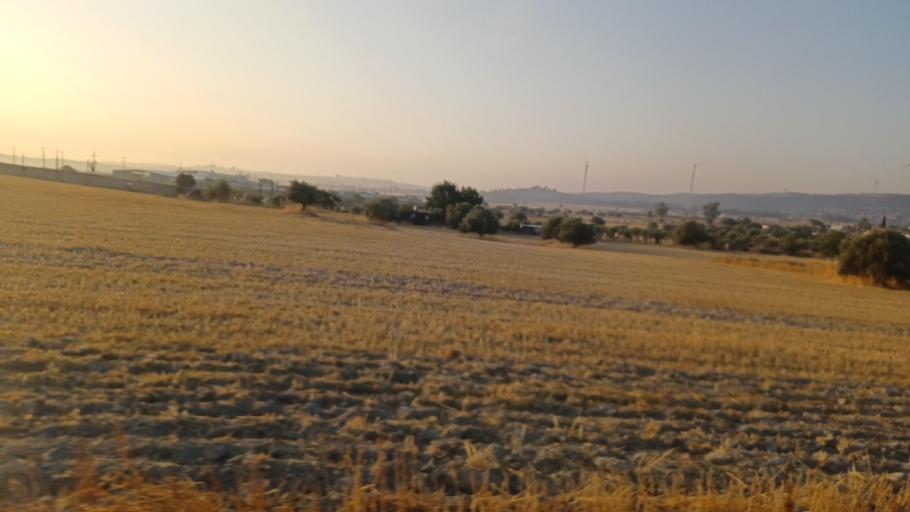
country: CY
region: Larnaka
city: Tersefanou
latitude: 34.8974
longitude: 33.5140
